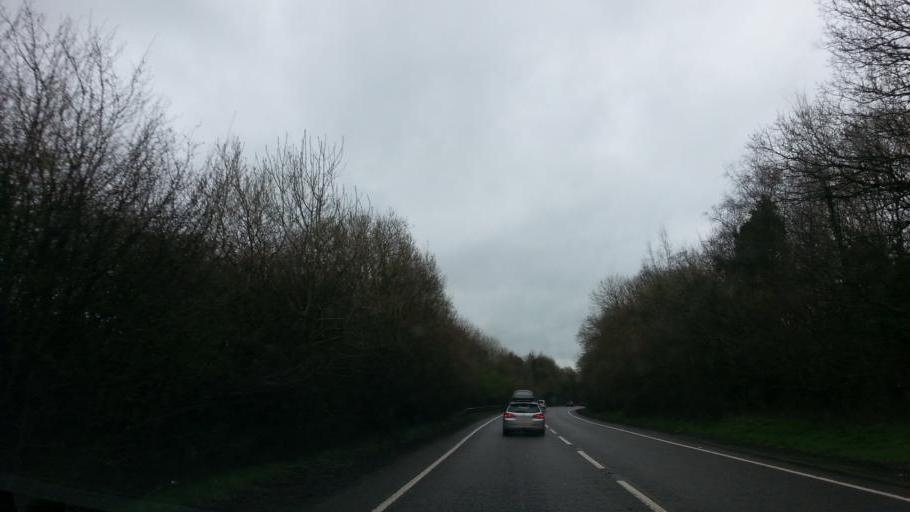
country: GB
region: England
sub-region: Devon
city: Barnstaple
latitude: 51.0527
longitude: -3.9520
